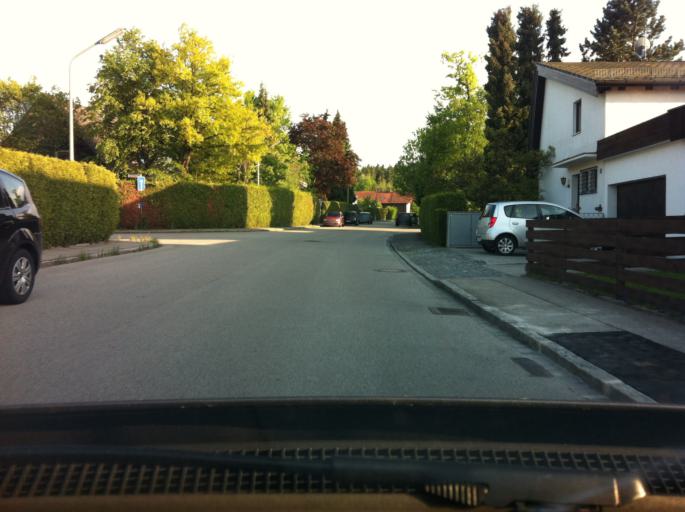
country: DE
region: Bavaria
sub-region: Upper Bavaria
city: Oberhaching
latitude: 48.0459
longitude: 11.5950
